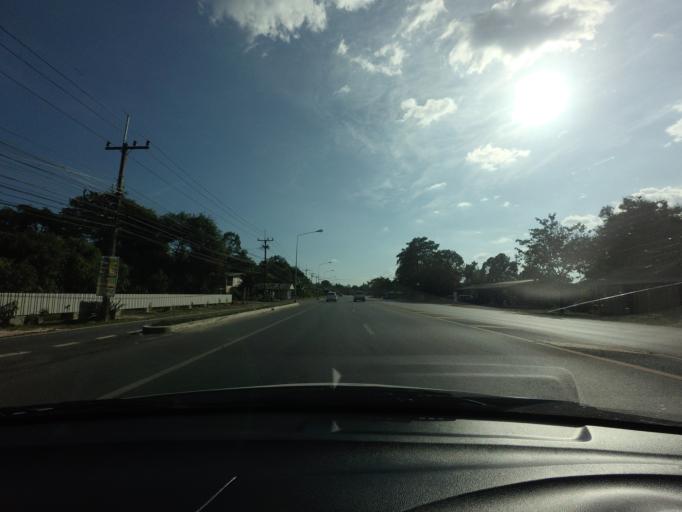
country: TH
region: Nakhon Nayok
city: Nakhon Nayok
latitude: 14.2695
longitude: 101.2730
